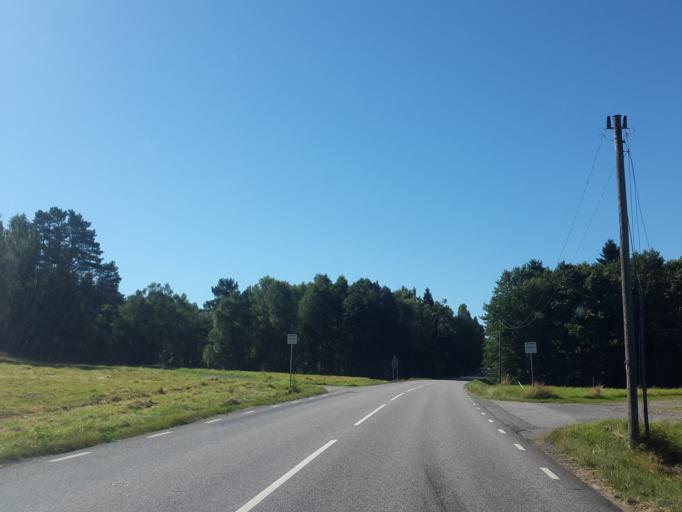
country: SE
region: Vaestra Goetaland
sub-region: Herrljunga Kommun
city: Herrljunga
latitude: 58.0620
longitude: 13.0431
